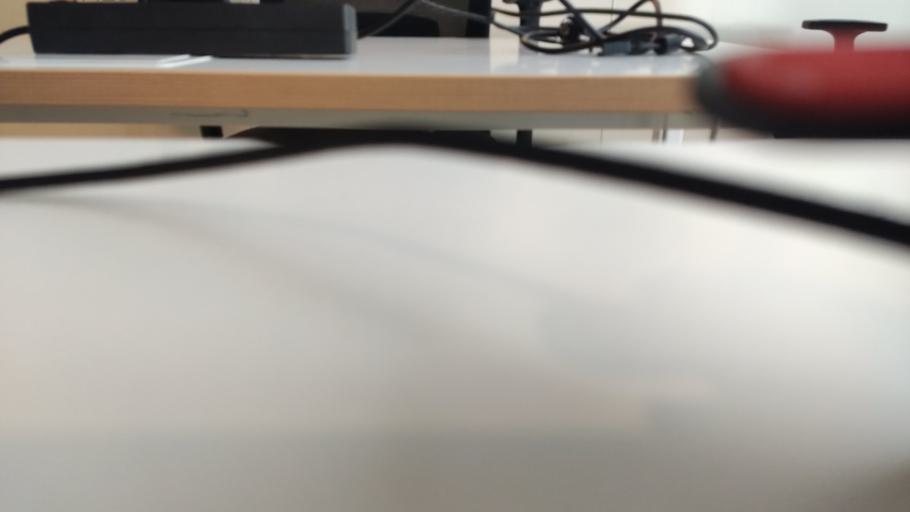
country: RU
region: Moskovskaya
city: Rogachevo
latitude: 56.4121
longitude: 37.0480
